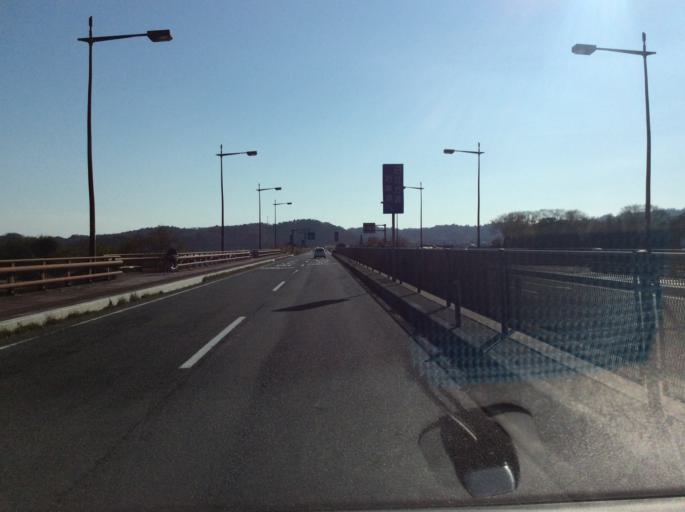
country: JP
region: Fukushima
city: Iwaki
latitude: 37.0609
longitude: 140.9409
